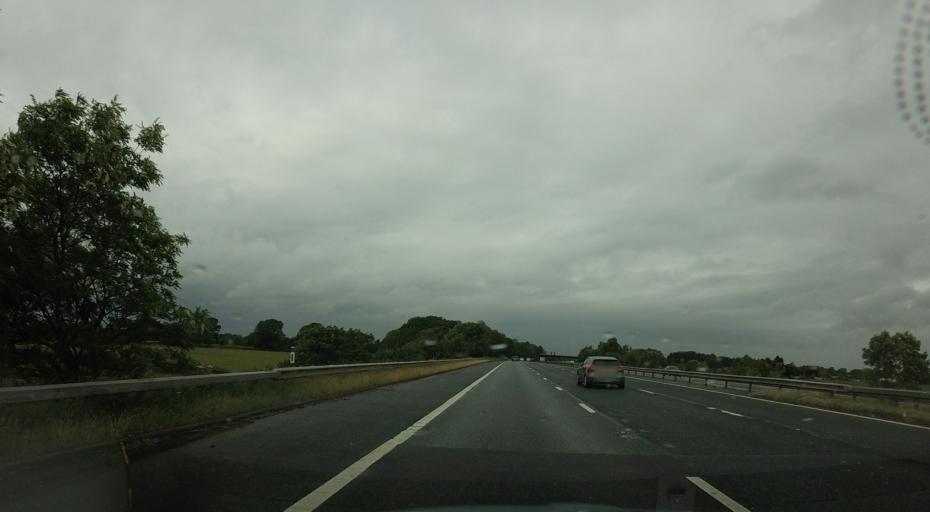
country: GB
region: England
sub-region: Cumbria
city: Scotby
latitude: 54.9101
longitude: -2.8968
